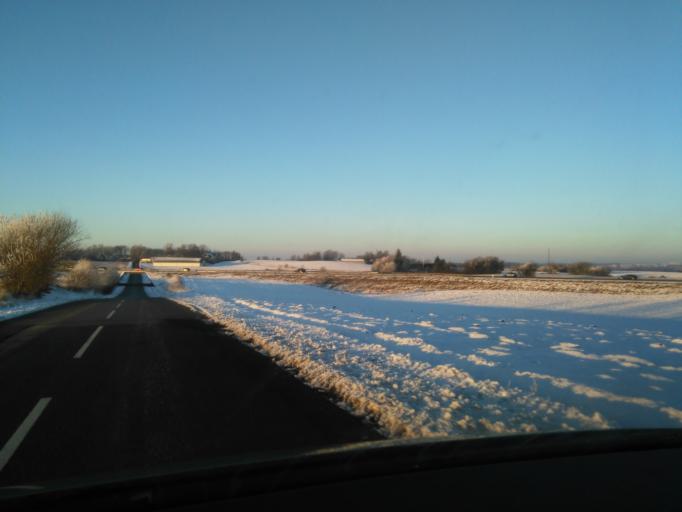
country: DK
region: Central Jutland
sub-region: Arhus Kommune
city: Stavtrup
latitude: 56.1158
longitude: 10.1057
